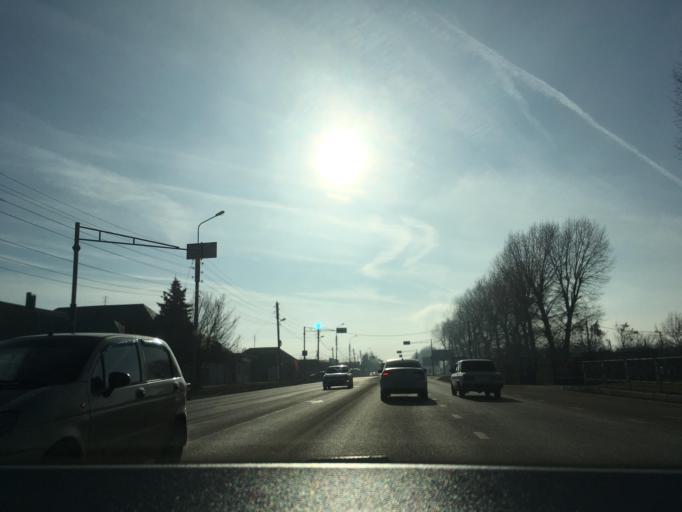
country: RU
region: Krasnodarskiy
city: Krasnodar
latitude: 45.1062
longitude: 39.0126
